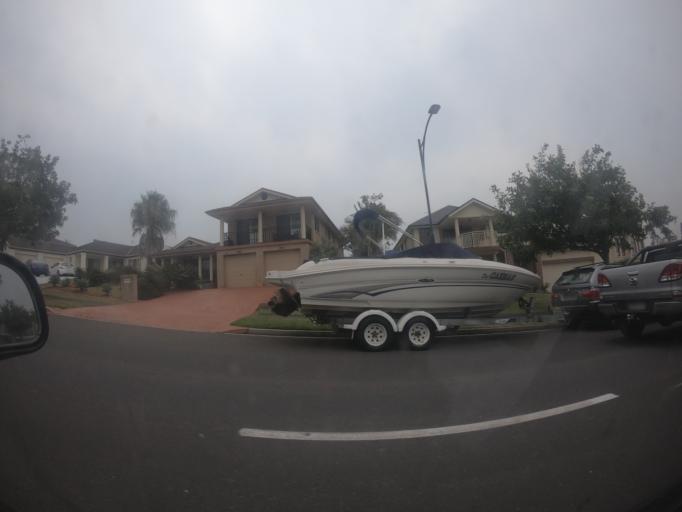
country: AU
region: New South Wales
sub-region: Shellharbour
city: Flinders
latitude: -34.5919
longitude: 150.8572
